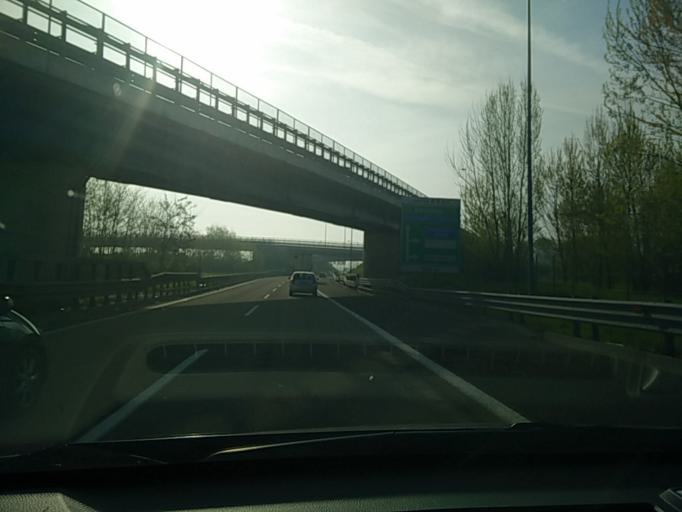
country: IT
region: Emilia-Romagna
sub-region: Provincia di Bologna
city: Bologna
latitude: 44.5193
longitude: 11.3699
